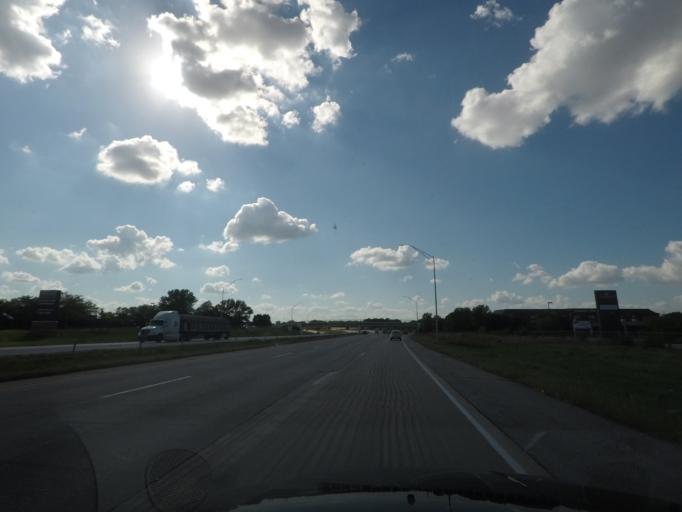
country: US
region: Iowa
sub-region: Polk County
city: Clive
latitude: 41.5923
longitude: -93.8018
